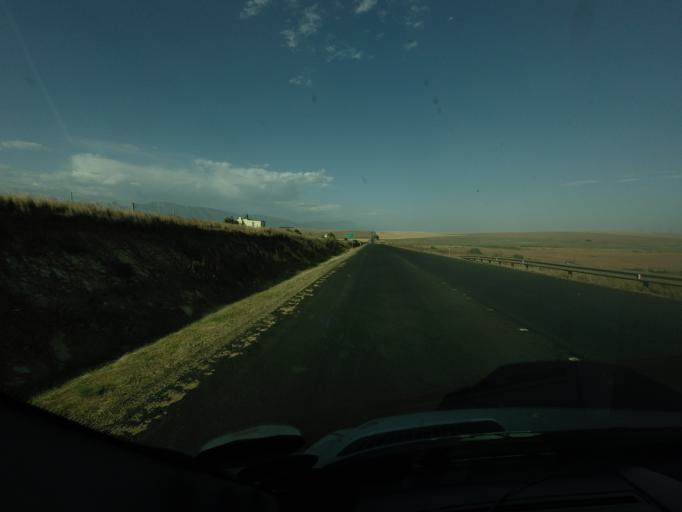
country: ZA
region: Western Cape
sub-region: Overberg District Municipality
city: Swellendam
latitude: -34.1071
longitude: 20.3546
